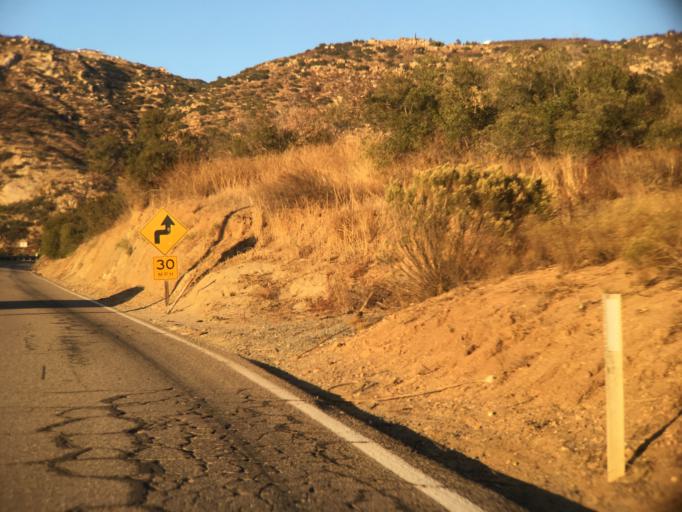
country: US
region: California
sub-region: San Diego County
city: Harbison Canyon
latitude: 32.8049
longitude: -116.8098
